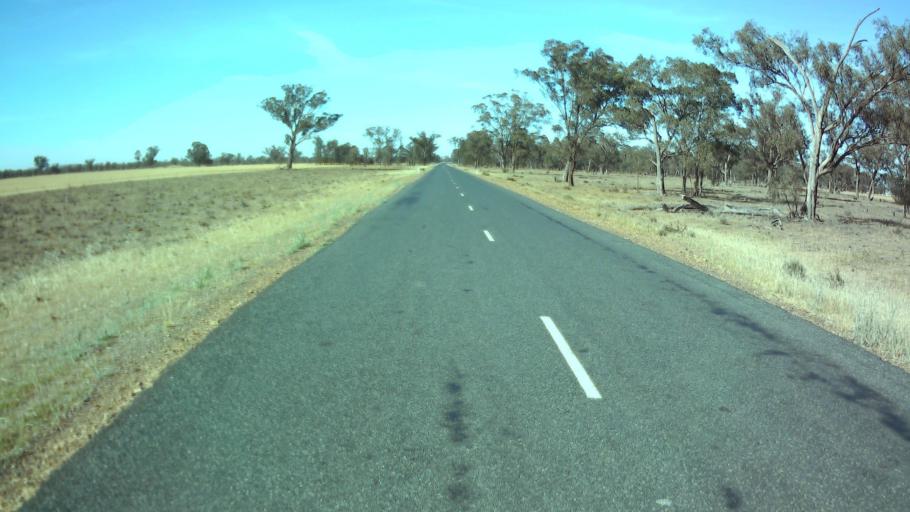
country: AU
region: New South Wales
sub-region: Weddin
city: Grenfell
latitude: -34.0876
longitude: 147.8912
